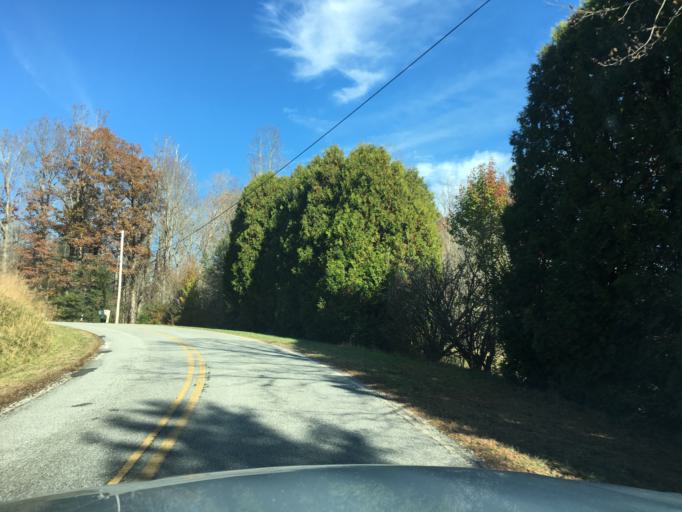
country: US
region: North Carolina
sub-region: Henderson County
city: Etowah
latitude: 35.3346
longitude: -82.6136
